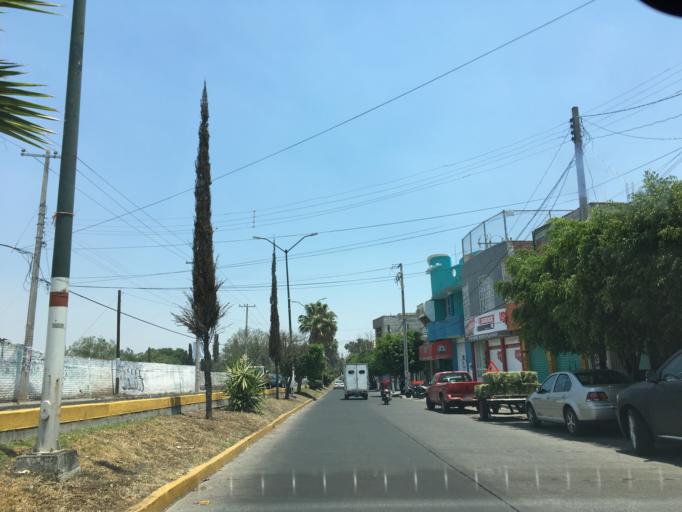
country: MX
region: Guanajuato
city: Uriangato
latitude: 20.1297
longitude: -101.1798
